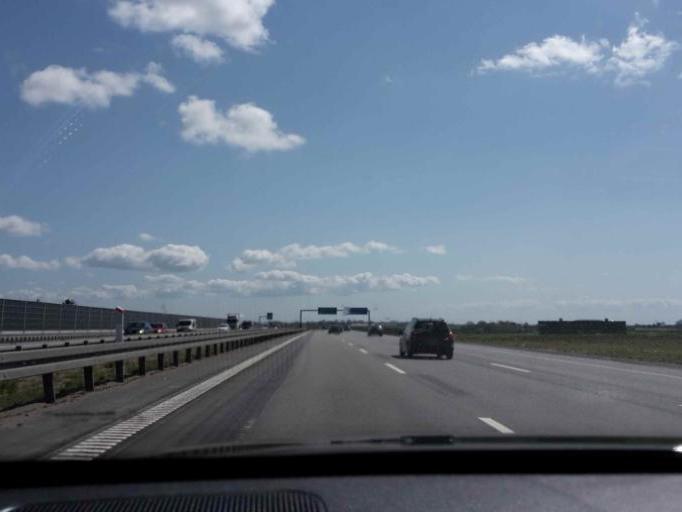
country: DK
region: South Denmark
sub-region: Middelfart Kommune
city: Strib
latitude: 55.5063
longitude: 9.7850
